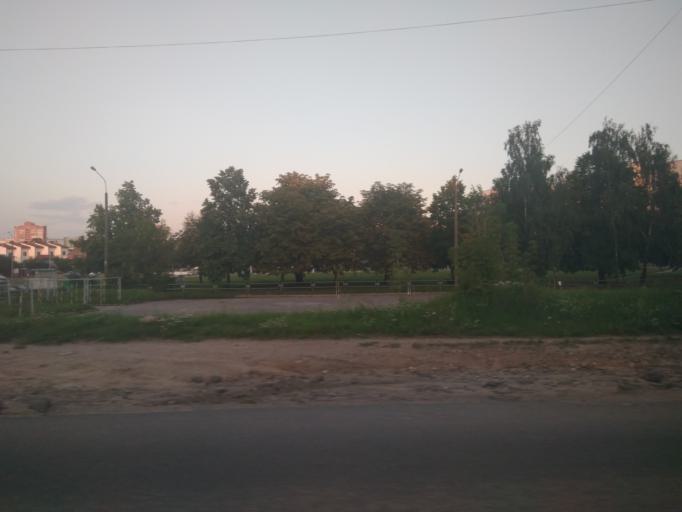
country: BY
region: Minsk
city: Novoye Medvezhino
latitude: 53.9254
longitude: 27.4750
